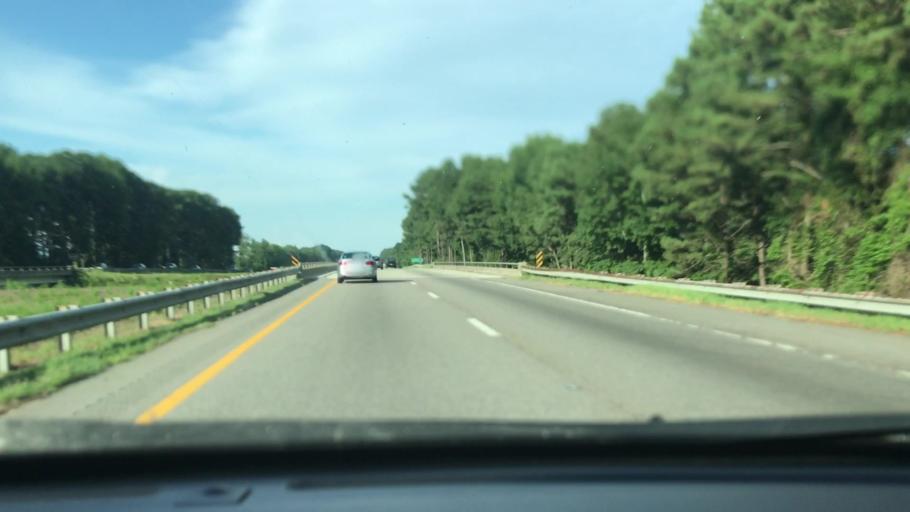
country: US
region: North Carolina
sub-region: Robeson County
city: Fairmont
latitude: 34.5599
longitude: -79.1811
